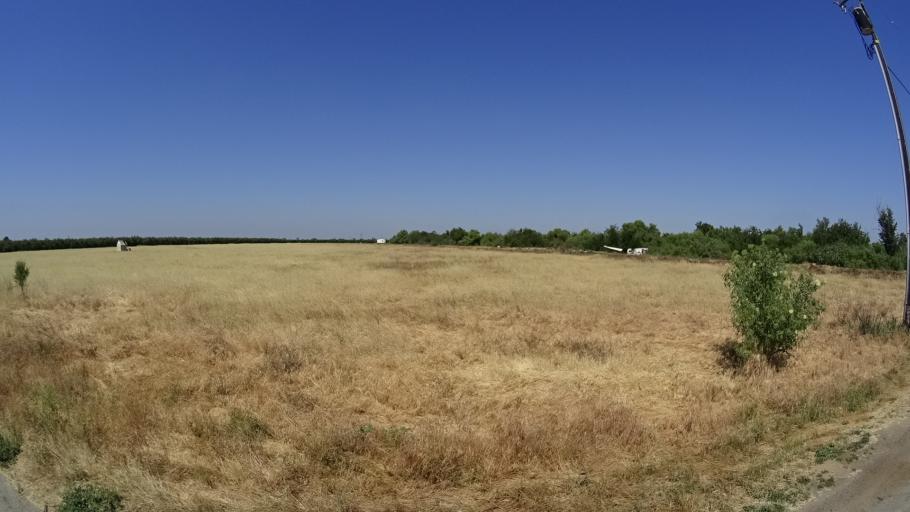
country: US
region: California
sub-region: Fresno County
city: Kingsburg
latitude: 36.4584
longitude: -119.5912
